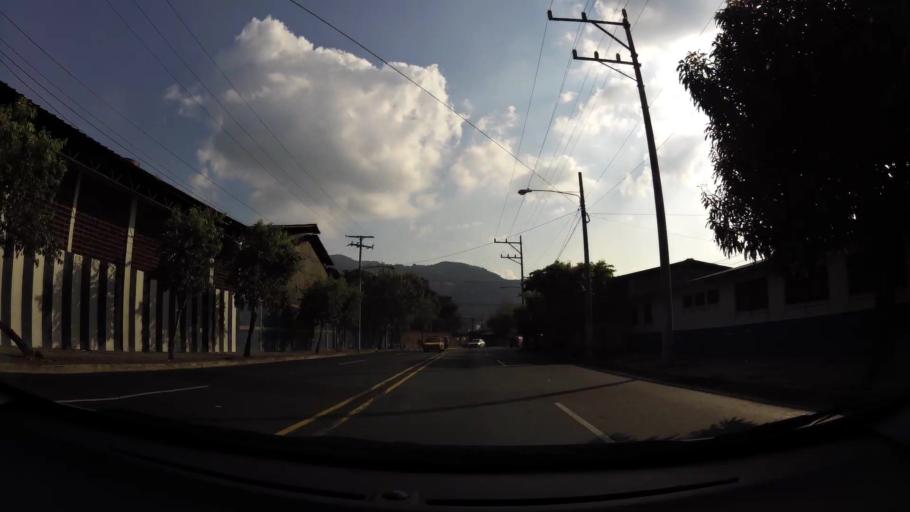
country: SV
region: San Salvador
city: San Salvador
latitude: 13.6973
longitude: -89.1748
